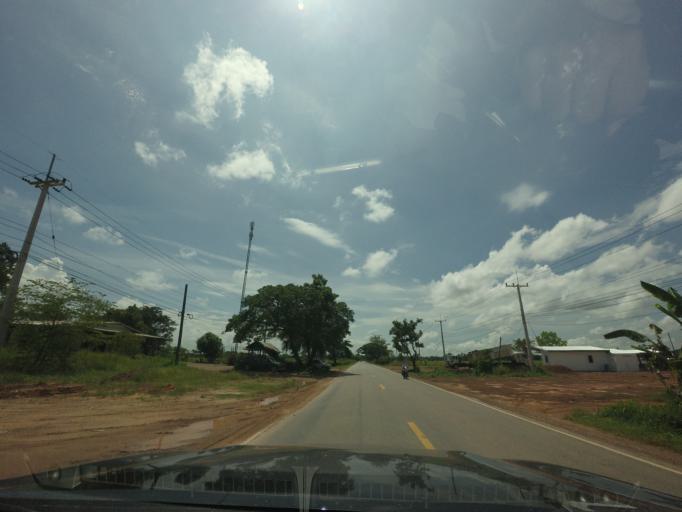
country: TH
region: Nong Khai
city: Pho Tak
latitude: 17.7682
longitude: 102.3966
